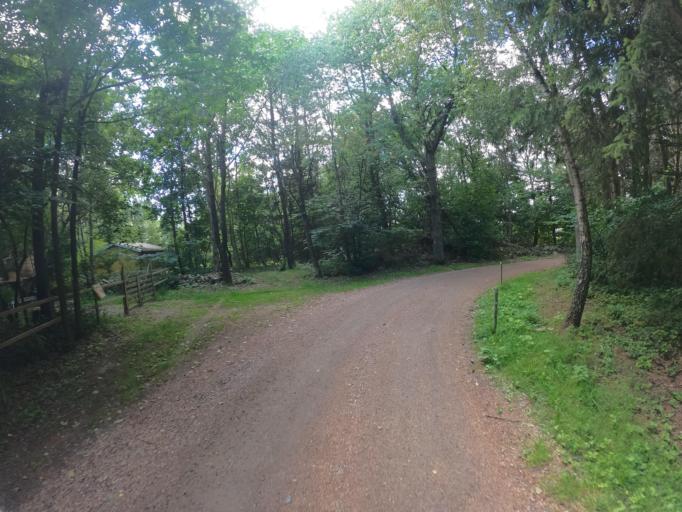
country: SE
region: Skane
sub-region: Lunds Kommun
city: Genarp
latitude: 55.6755
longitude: 13.3613
